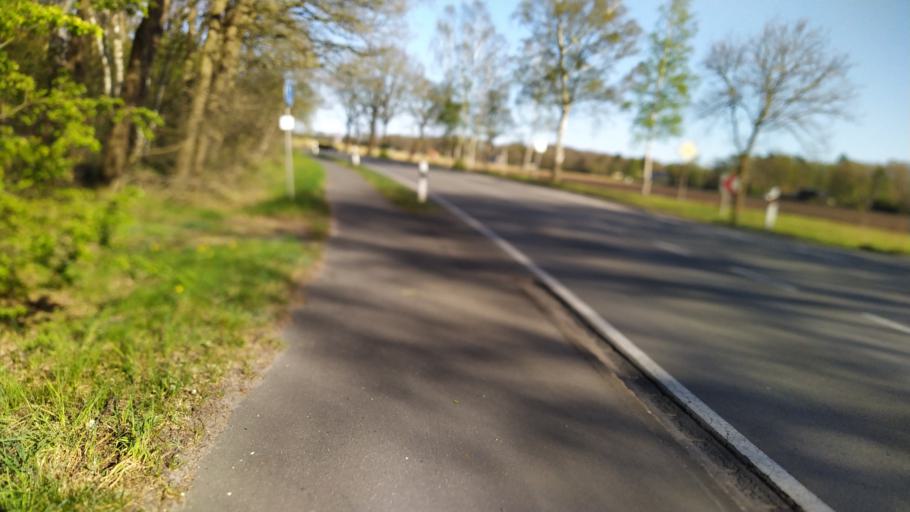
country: DE
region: Lower Saxony
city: Hamersen
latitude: 53.2801
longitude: 9.4790
